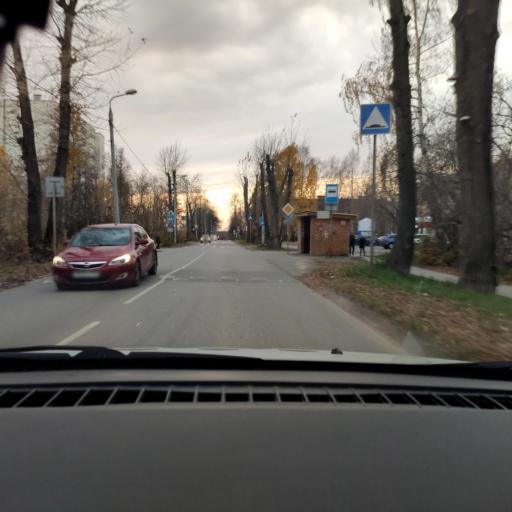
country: RU
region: Perm
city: Perm
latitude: 58.1202
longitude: 56.3849
